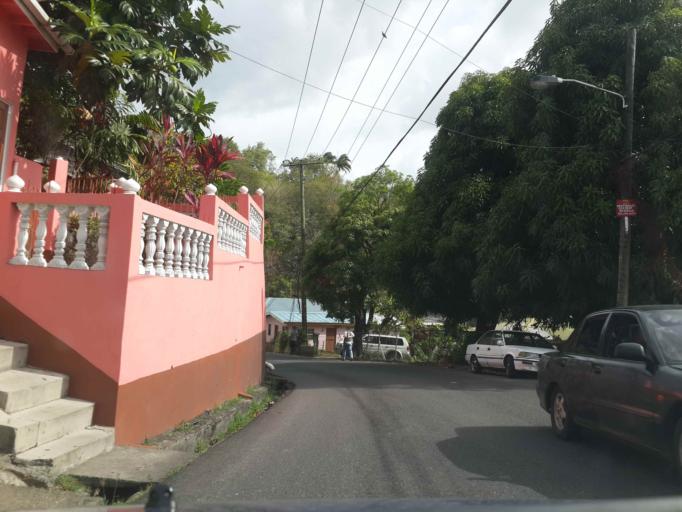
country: LC
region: Castries Quarter
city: Bisee
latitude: 14.0172
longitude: -60.9861
